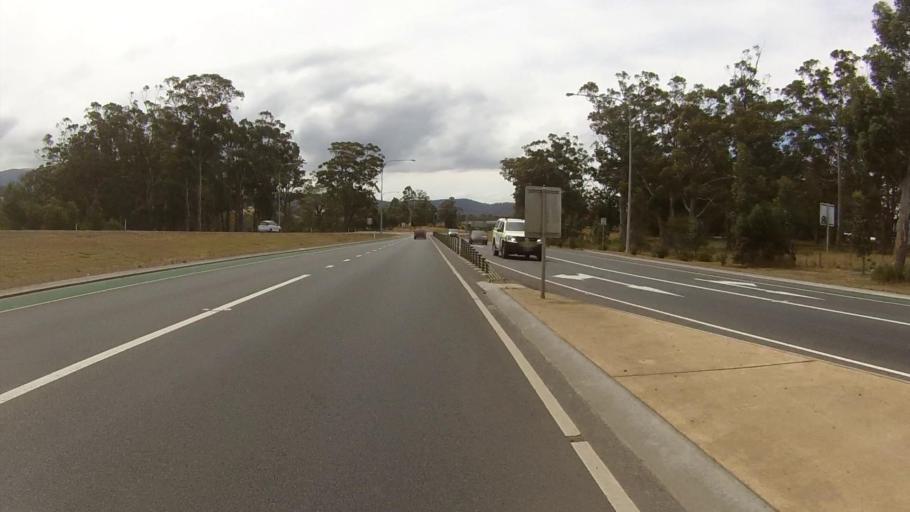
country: AU
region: Tasmania
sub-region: Kingborough
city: Kingston
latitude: -42.9866
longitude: 147.2890
